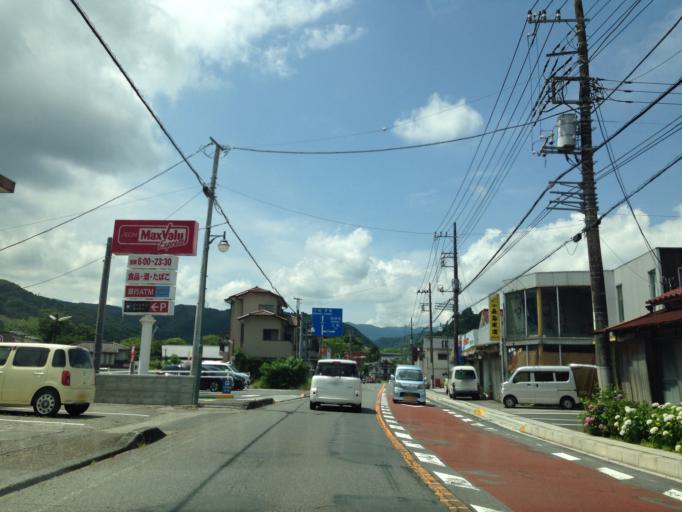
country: JP
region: Shizuoka
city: Heda
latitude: 34.9299
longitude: 138.9333
